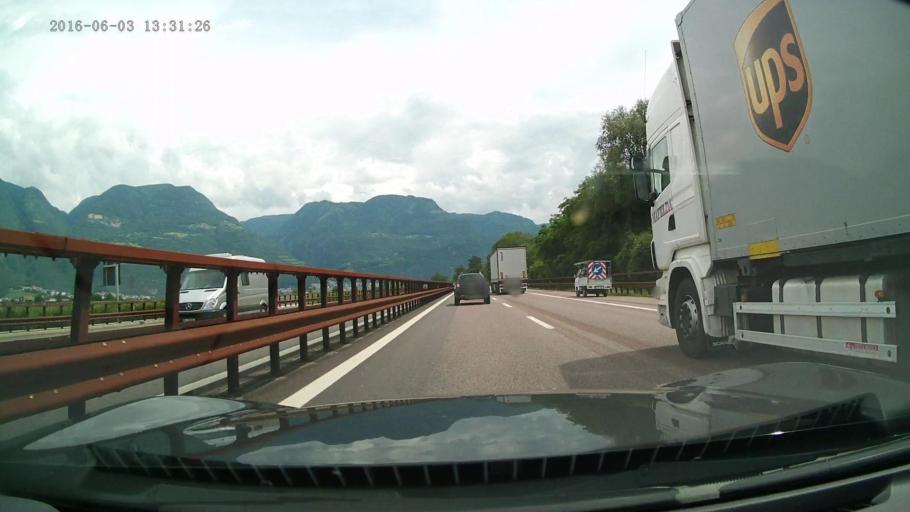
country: IT
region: Trentino-Alto Adige
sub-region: Bolzano
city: San Giacomo
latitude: 46.4513
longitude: 11.3077
